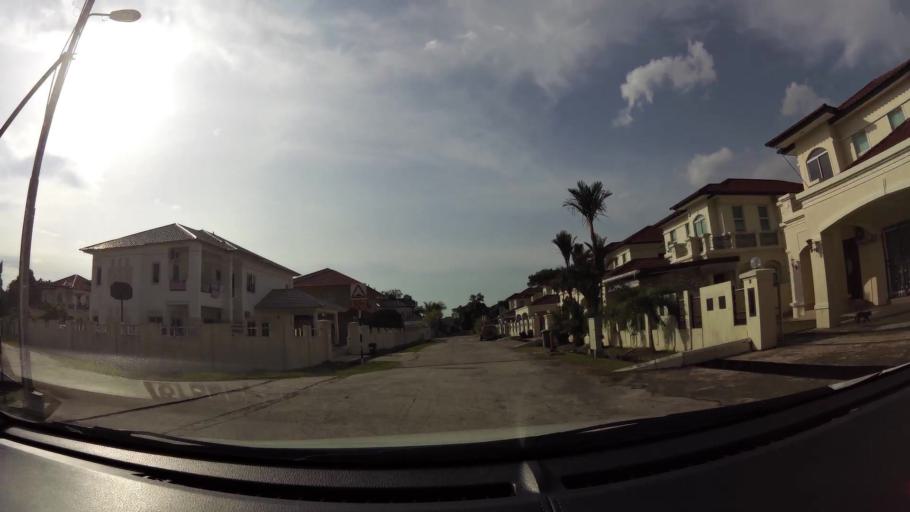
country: BN
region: Brunei and Muara
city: Bandar Seri Begawan
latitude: 4.9673
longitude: 114.9732
